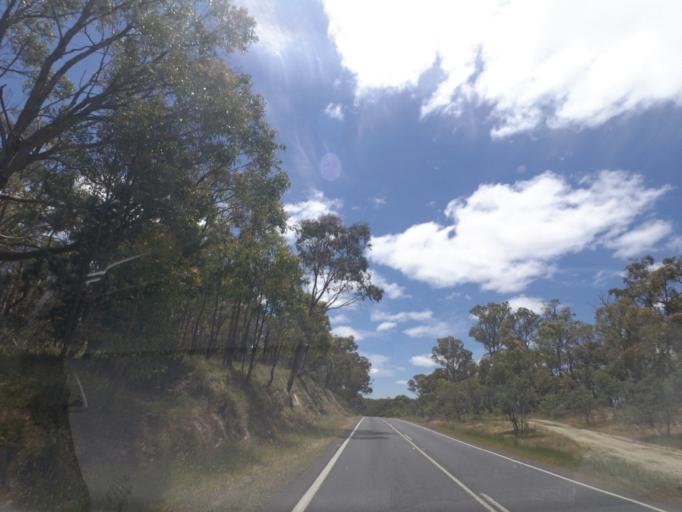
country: AU
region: Victoria
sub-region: Mount Alexander
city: Castlemaine
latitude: -37.2927
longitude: 144.1630
